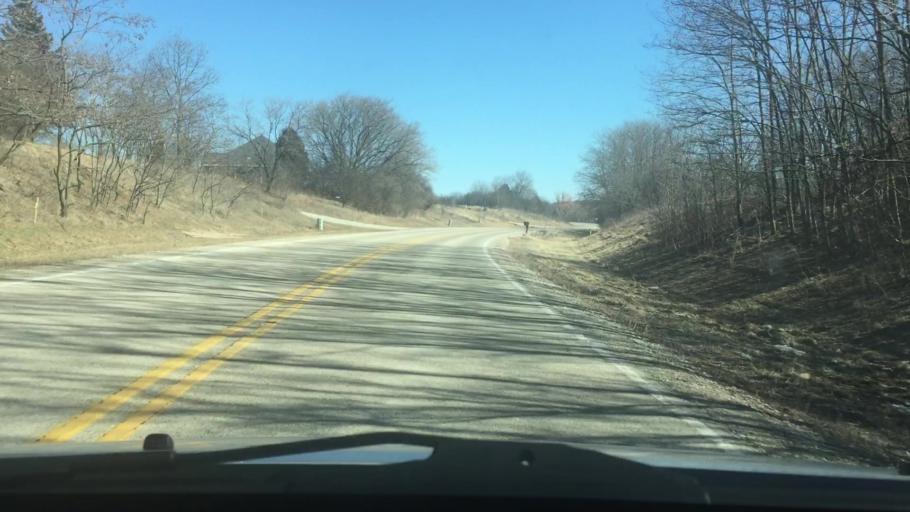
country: US
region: Wisconsin
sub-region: Waukesha County
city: Hartland
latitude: 43.1048
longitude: -88.3179
